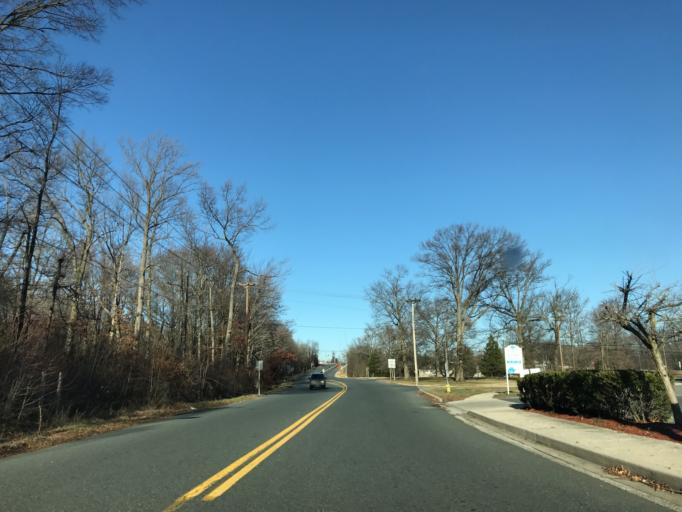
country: US
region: Maryland
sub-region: Harford County
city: Aberdeen
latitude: 39.5135
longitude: -76.1633
